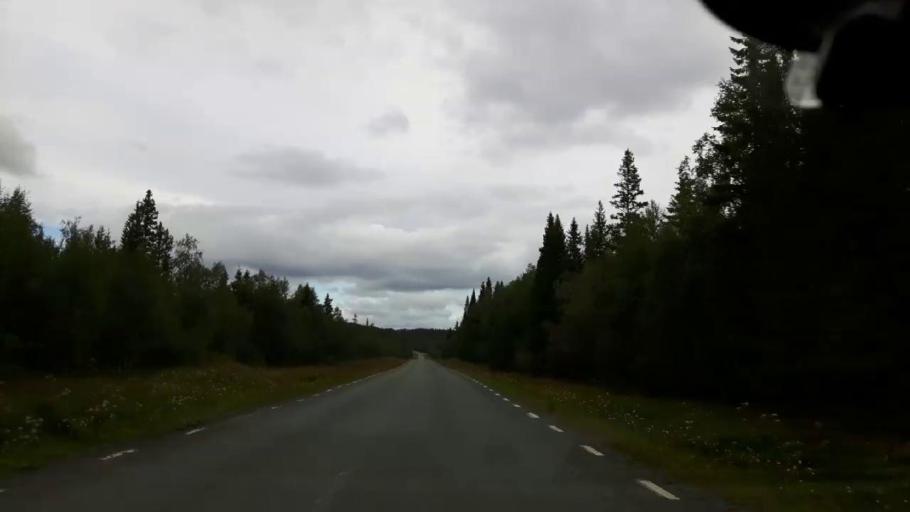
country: SE
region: Jaemtland
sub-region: Krokoms Kommun
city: Valla
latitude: 63.5614
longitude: 13.8474
